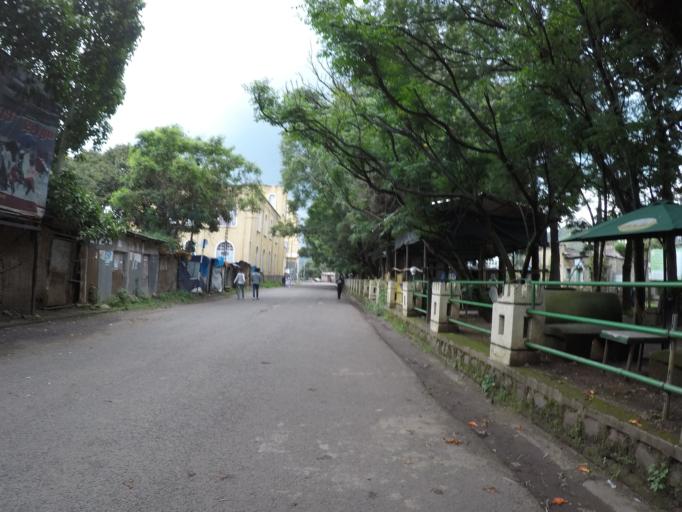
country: ET
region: Amhara
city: Gondar
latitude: 12.6145
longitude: 37.4730
